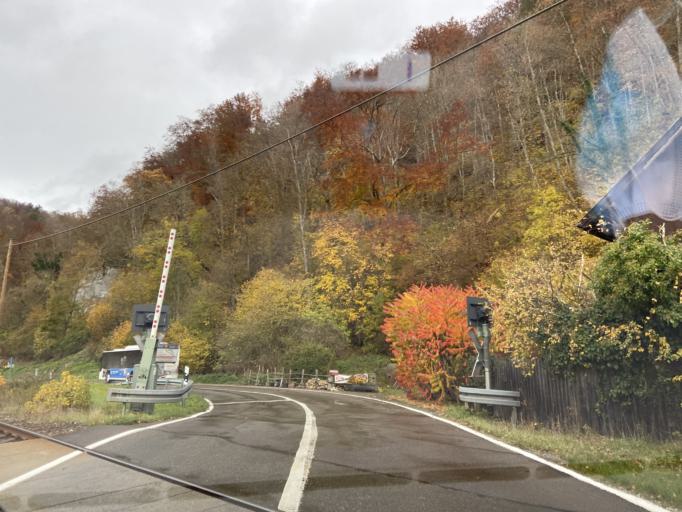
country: DE
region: Baden-Wuerttemberg
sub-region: Tuebingen Region
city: Stetten am Kalten Markt
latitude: 48.0844
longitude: 9.0776
